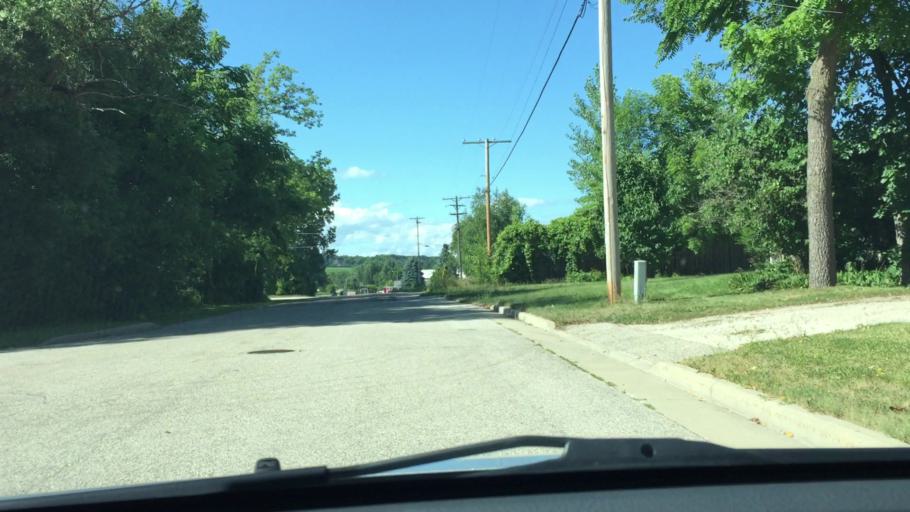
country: US
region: Wisconsin
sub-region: Waukesha County
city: Pewaukee
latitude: 43.0852
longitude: -88.2548
